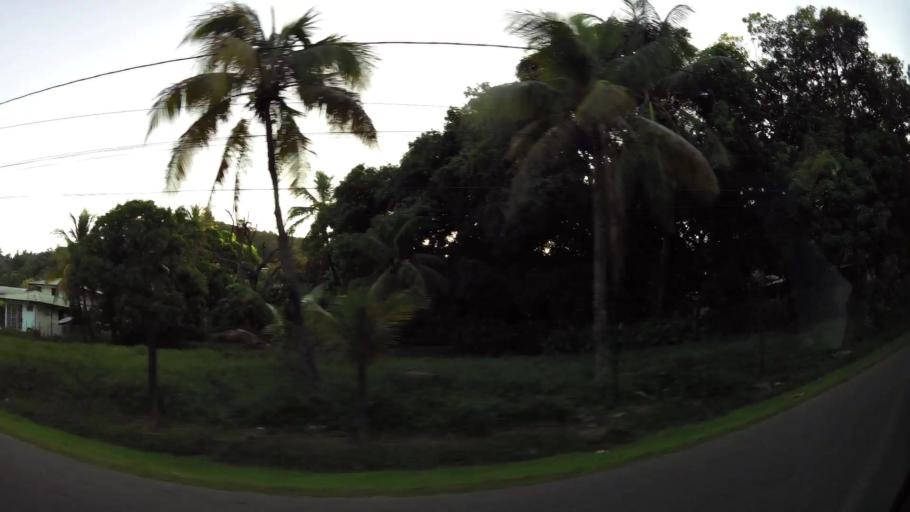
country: GF
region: Guyane
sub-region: Guyane
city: Cayenne
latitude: 4.9236
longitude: -52.3039
